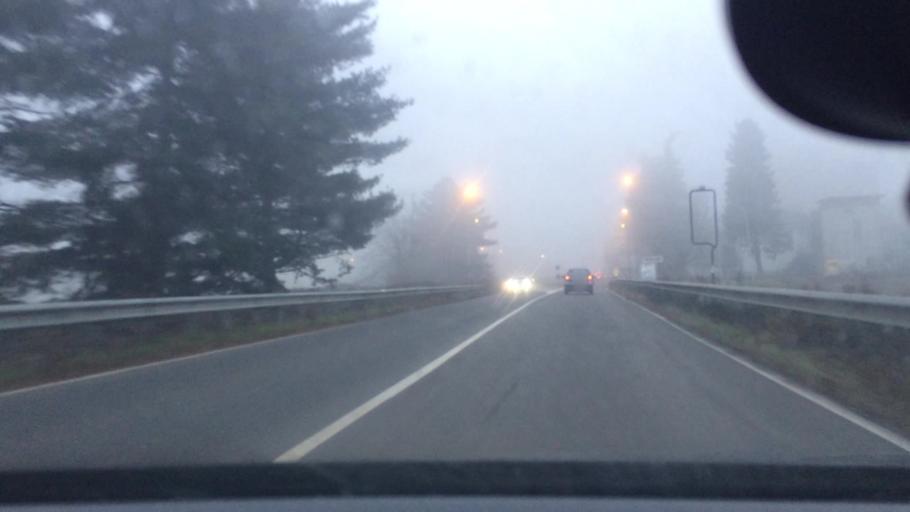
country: IT
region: Lombardy
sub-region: Citta metropolitana di Milano
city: Nerviano
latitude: 45.5556
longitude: 8.9893
